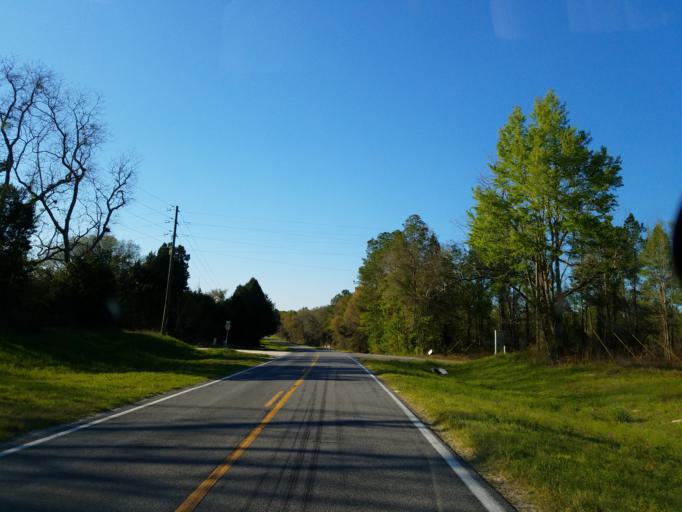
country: US
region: Florida
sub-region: Suwannee County
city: Live Oak
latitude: 30.2285
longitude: -82.9405
